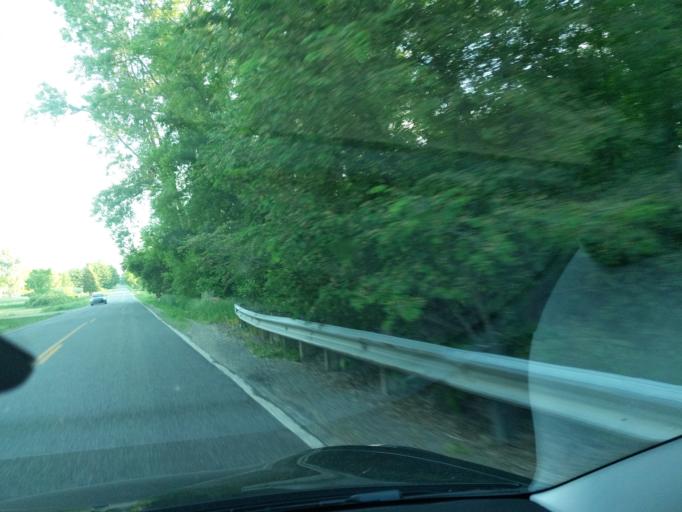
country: US
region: Michigan
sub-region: Barry County
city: Nashville
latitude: 42.5586
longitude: -85.0940
